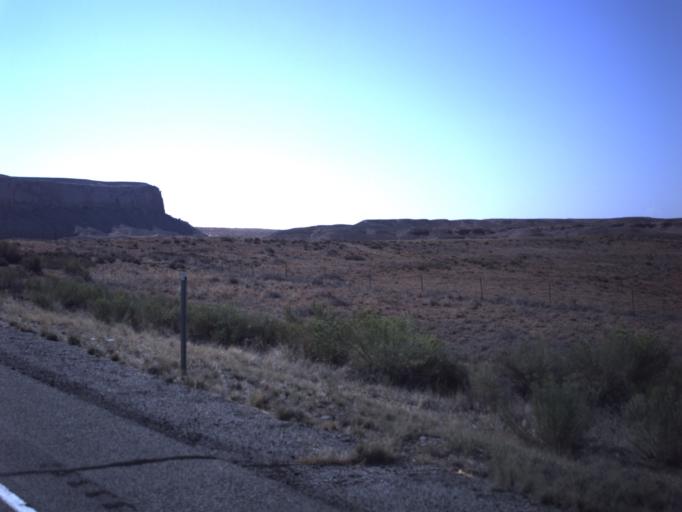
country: US
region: Utah
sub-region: San Juan County
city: Blanding
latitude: 37.2521
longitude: -109.6129
